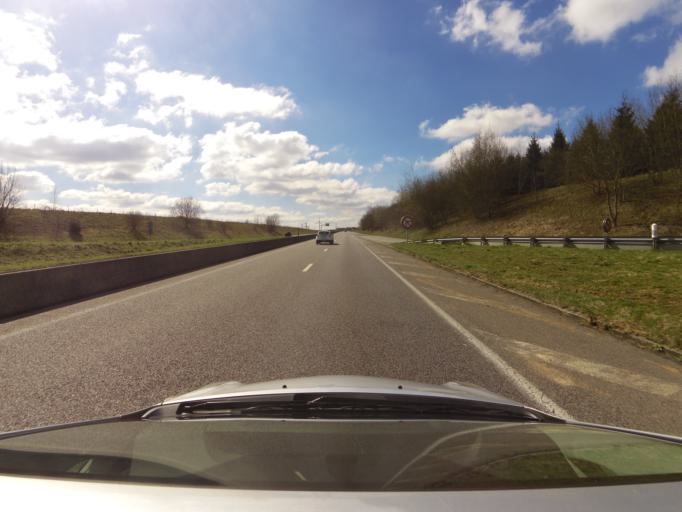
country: FR
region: Haute-Normandie
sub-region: Departement de la Seine-Maritime
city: Foucarmont
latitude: 49.8297
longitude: 1.5248
